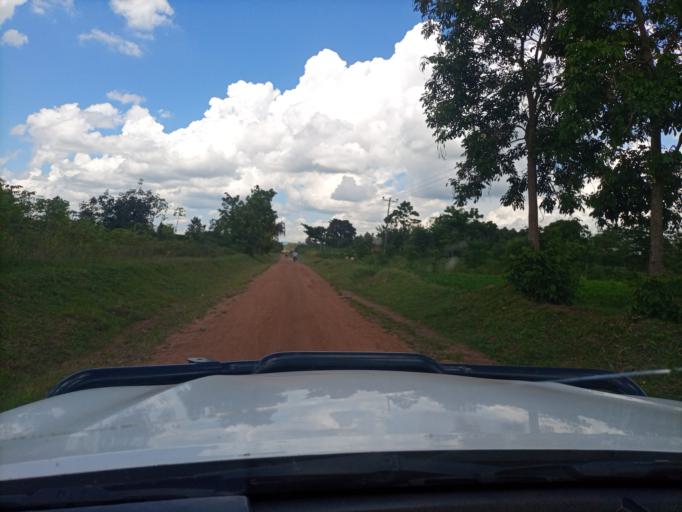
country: UG
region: Eastern Region
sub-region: Tororo District
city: Tororo
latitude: 0.6760
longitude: 34.0057
